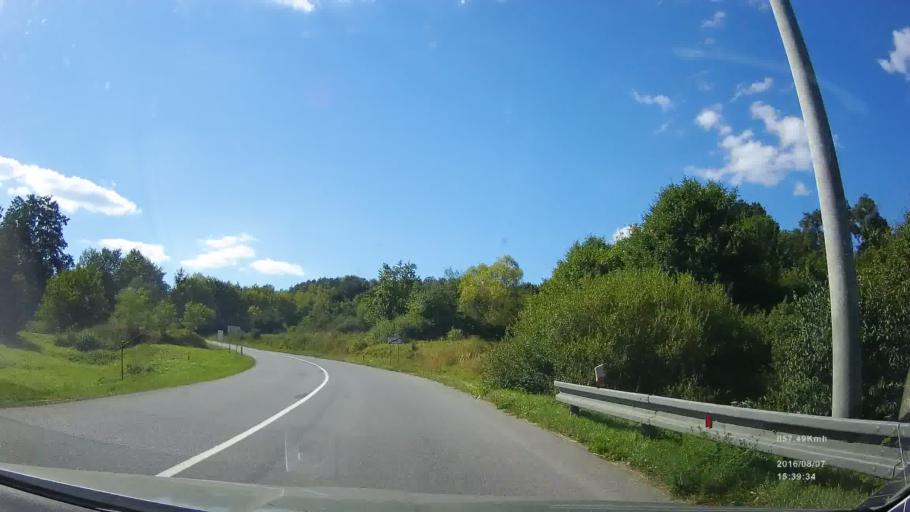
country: SK
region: Presovsky
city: Giraltovce
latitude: 49.1190
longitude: 21.6028
